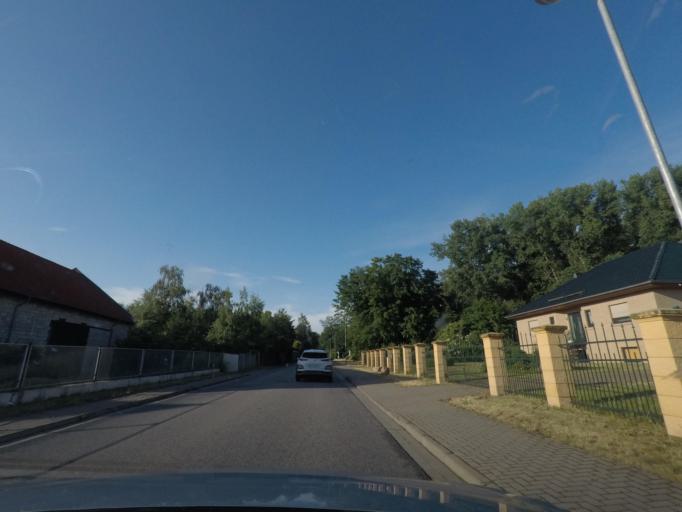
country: DE
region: Saxony-Anhalt
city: Huy-Neinstedt
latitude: 52.0139
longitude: 10.8982
